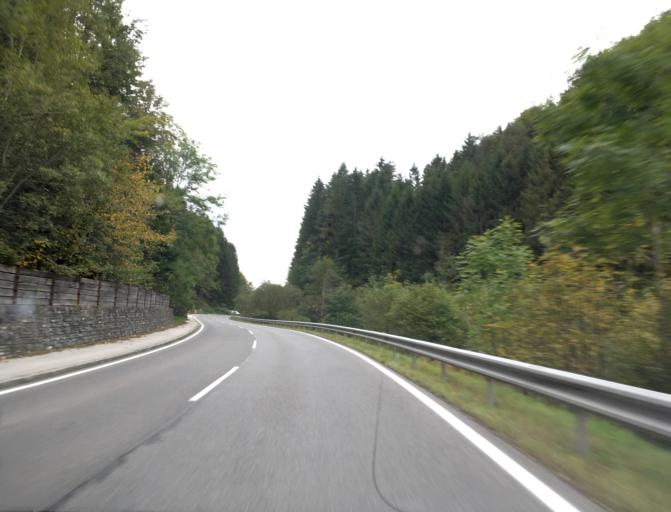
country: AT
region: Lower Austria
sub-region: Politischer Bezirk Neunkirchen
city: Edlitz
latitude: 47.5795
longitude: 16.1424
